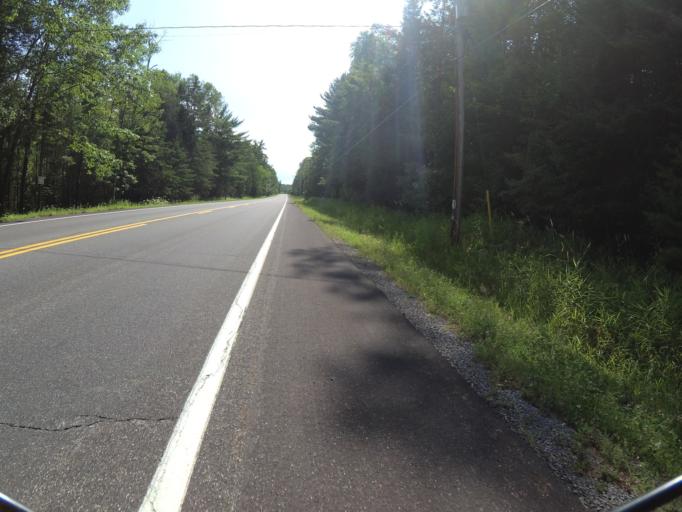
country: CA
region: Ontario
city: Arnprior
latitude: 45.5002
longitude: -76.1274
